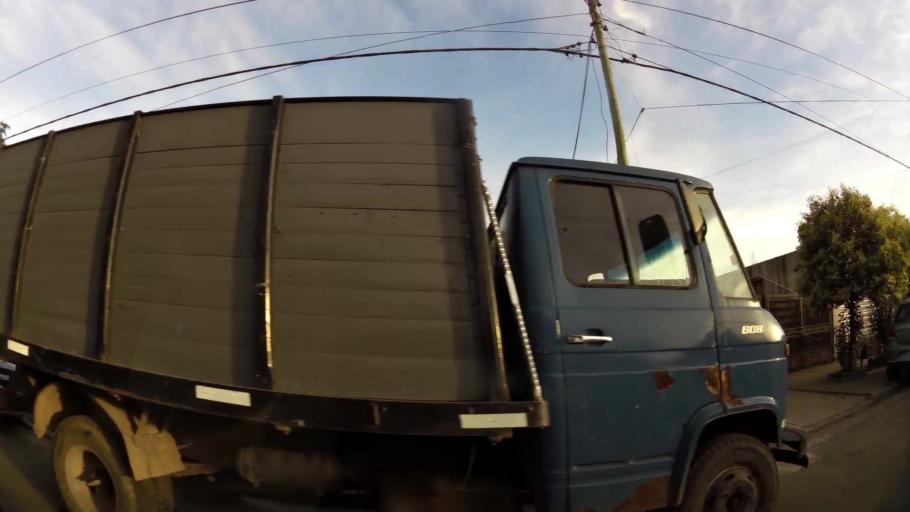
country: AR
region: Buenos Aires
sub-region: Partido de Almirante Brown
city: Adrogue
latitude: -34.7891
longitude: -58.3451
